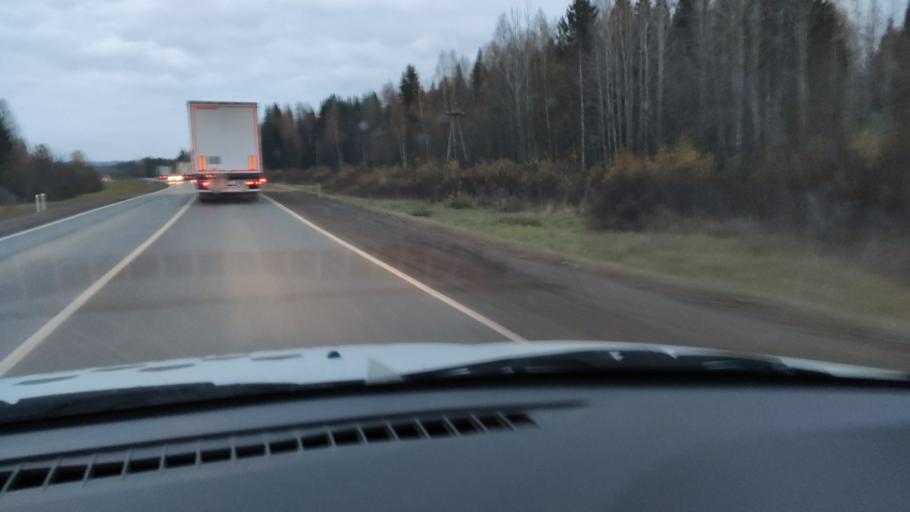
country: RU
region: Kirov
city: Kostino
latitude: 58.8556
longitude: 53.1955
